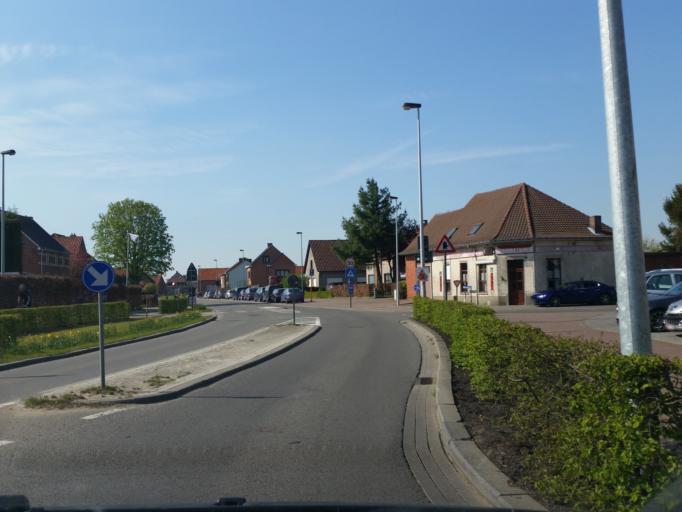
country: BE
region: Flanders
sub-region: Provincie Oost-Vlaanderen
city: Sint-Gillis-Waas
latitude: 51.2056
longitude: 4.1471
